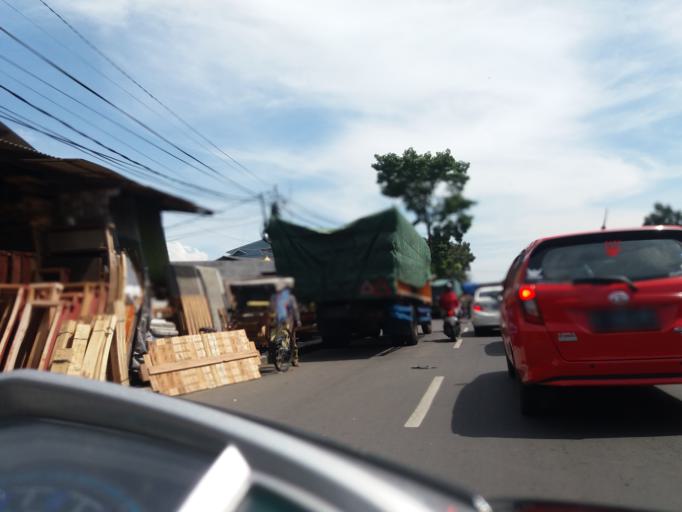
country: ID
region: West Java
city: Bandung
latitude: -6.9487
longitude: 107.6132
